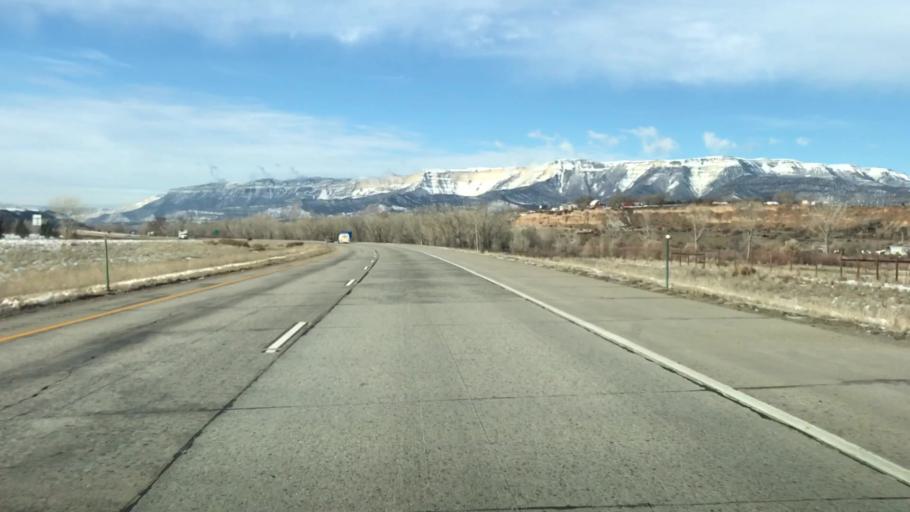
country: US
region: Colorado
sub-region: Garfield County
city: Rifle
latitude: 39.5263
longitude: -107.7649
